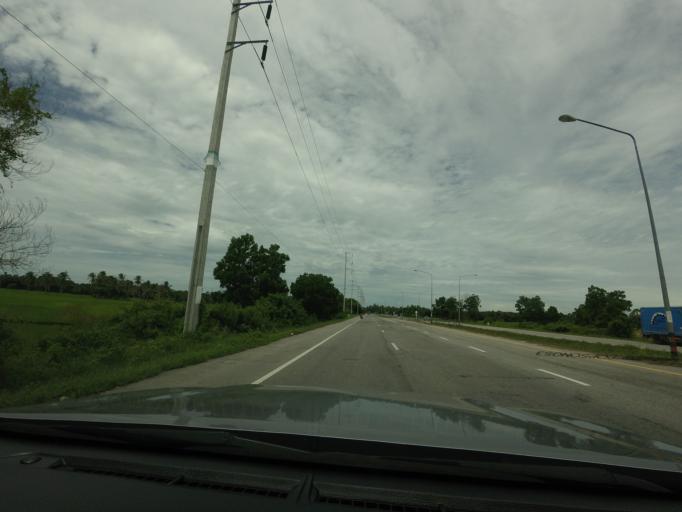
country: TH
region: Pattani
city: Nong Chik
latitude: 6.8324
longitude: 101.2190
